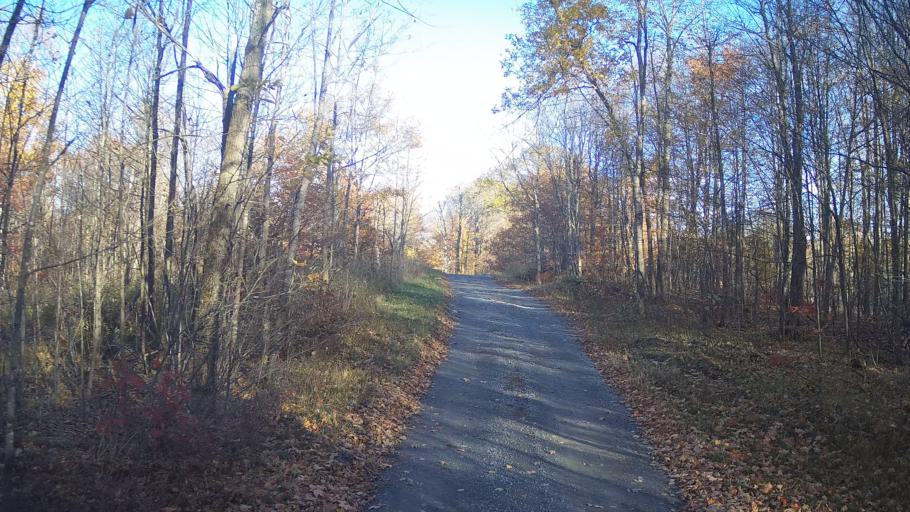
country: CA
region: Ontario
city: Perth
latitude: 44.7353
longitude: -76.4287
